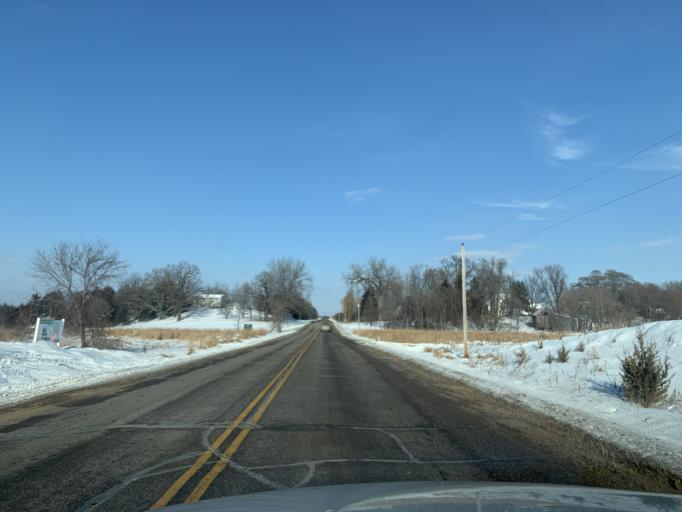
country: US
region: Minnesota
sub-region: Wright County
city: Buffalo
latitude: 45.1962
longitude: -93.8271
